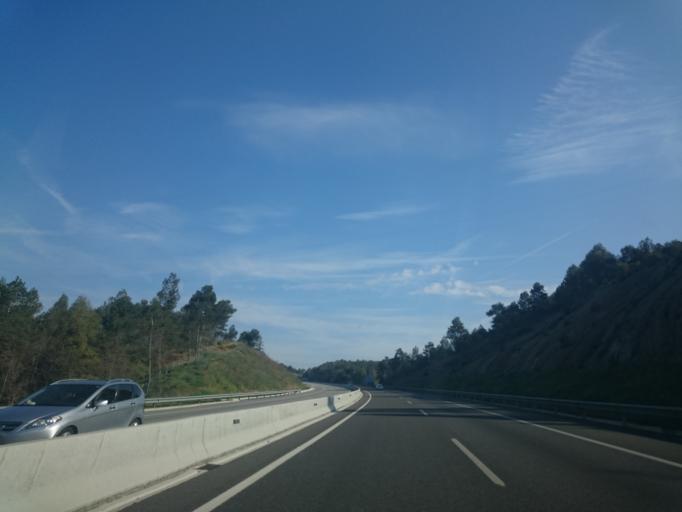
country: ES
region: Catalonia
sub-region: Provincia de Barcelona
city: Avinyo
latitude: 41.8427
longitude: 1.9827
